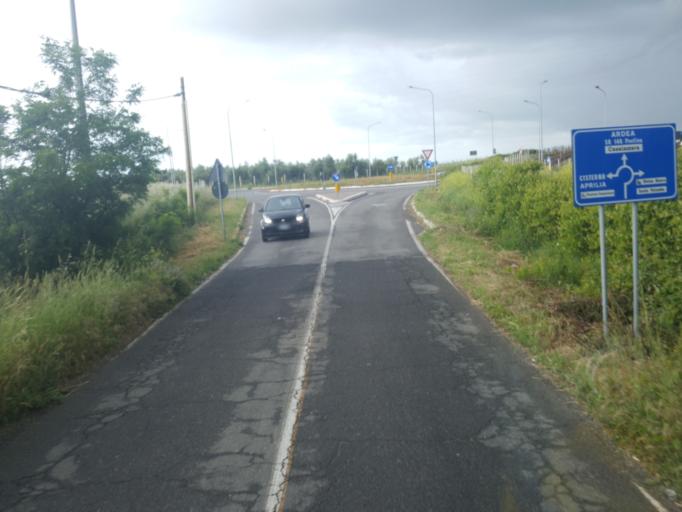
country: IT
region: Latium
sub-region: Citta metropolitana di Roma Capitale
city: Mantiglia di Ardea
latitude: 41.6593
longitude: 12.6289
